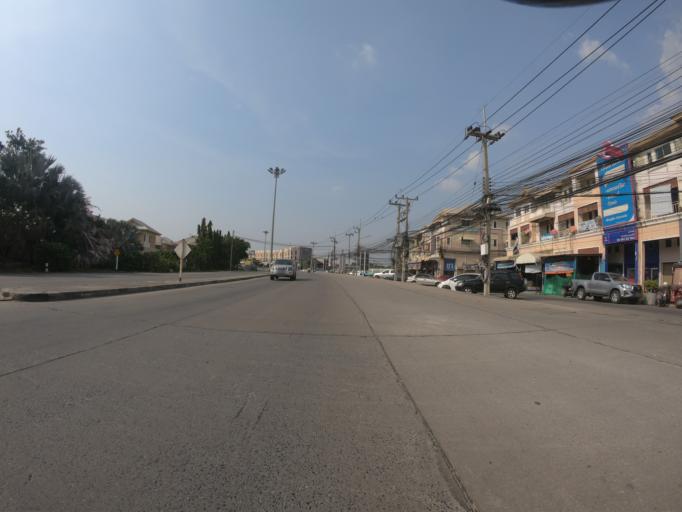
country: TH
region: Phra Nakhon Si Ayutthaya
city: Phra Nakhon Si Ayutthaya
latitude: 14.3372
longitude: 100.6043
